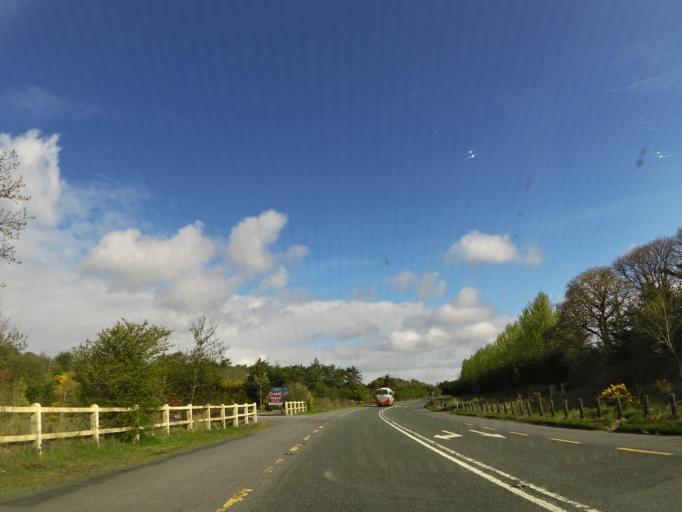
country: IE
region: Connaught
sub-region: Maigh Eo
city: Swinford
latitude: 53.8616
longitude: -8.8552
